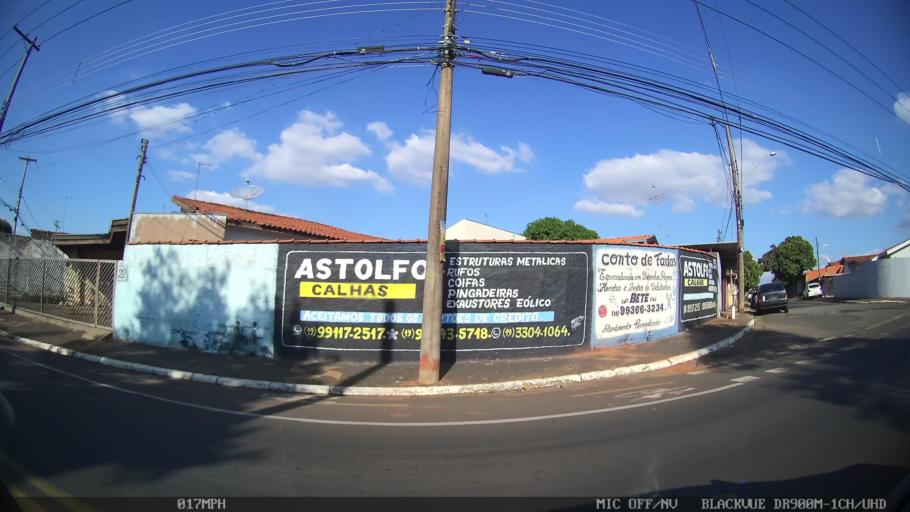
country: BR
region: Sao Paulo
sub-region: Nova Odessa
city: Nova Odessa
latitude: -22.7880
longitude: -47.3028
